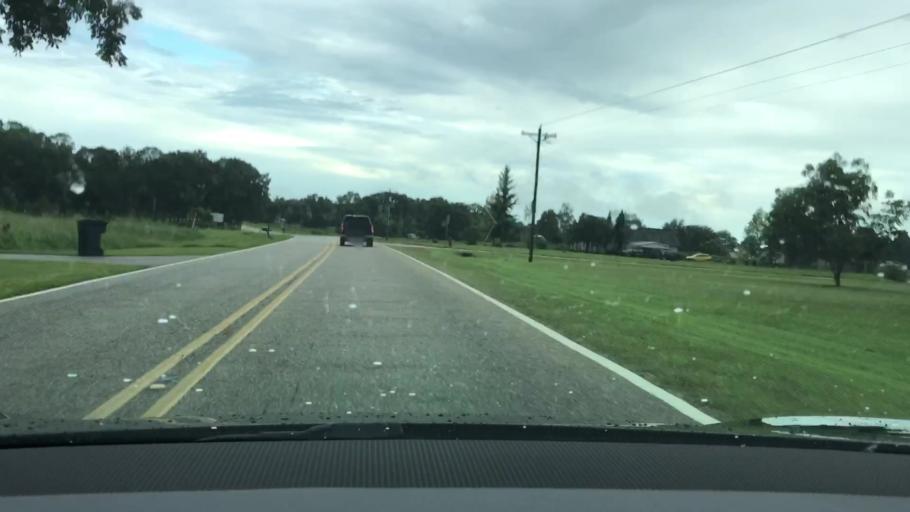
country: US
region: Alabama
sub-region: Geneva County
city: Samson
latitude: 31.1207
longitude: -86.1241
